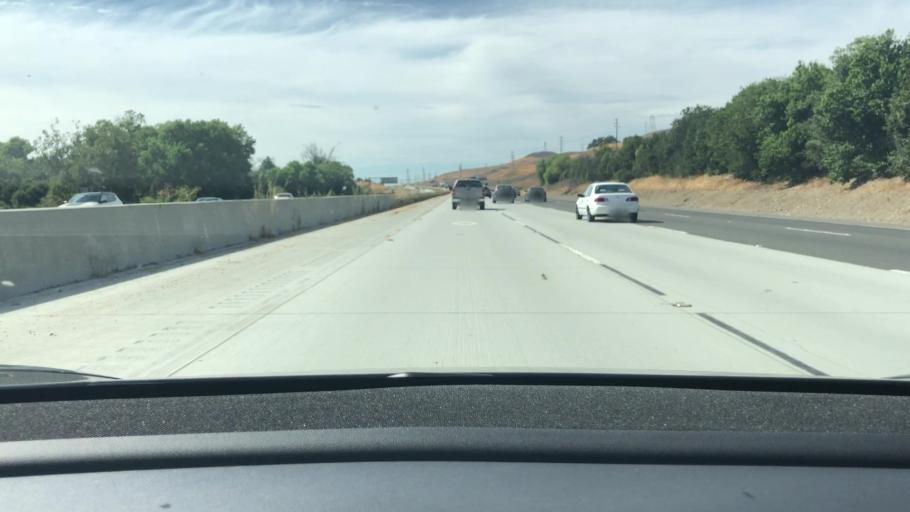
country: US
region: California
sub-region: Santa Clara County
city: Morgan Hill
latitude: 37.2132
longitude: -121.7264
